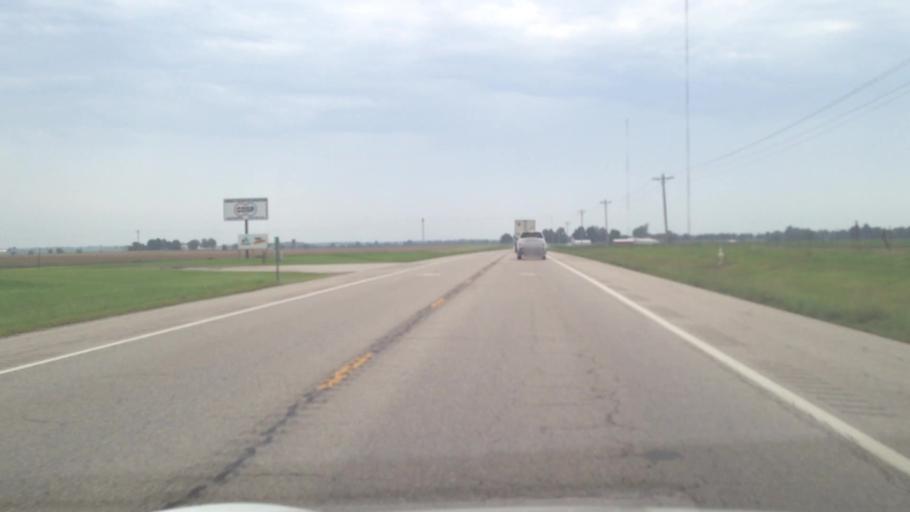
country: US
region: Missouri
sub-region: Jasper County
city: Carl Junction
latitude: 37.2318
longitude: -94.7050
